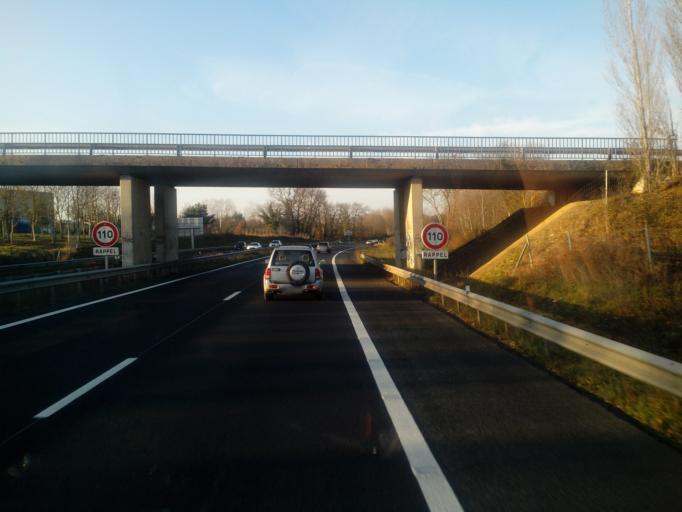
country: FR
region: Limousin
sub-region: Departement de la Correze
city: Saint-Pantaleon-de-Larche
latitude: 45.1403
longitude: 1.4886
